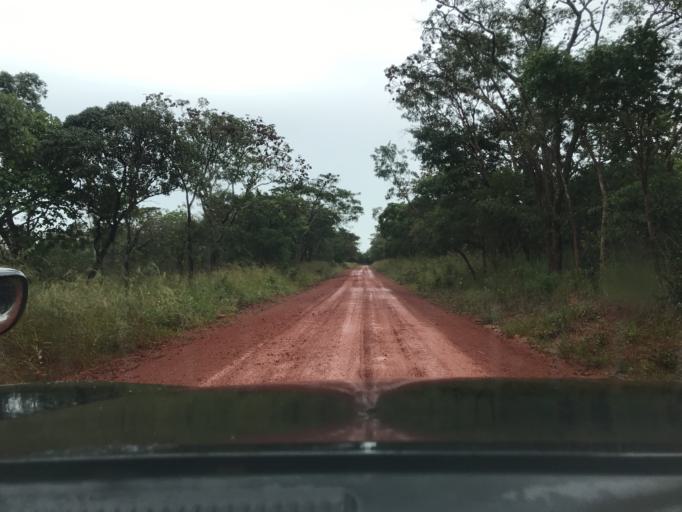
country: TZ
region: Kigoma
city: Uvinza
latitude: -5.2885
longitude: 30.3691
